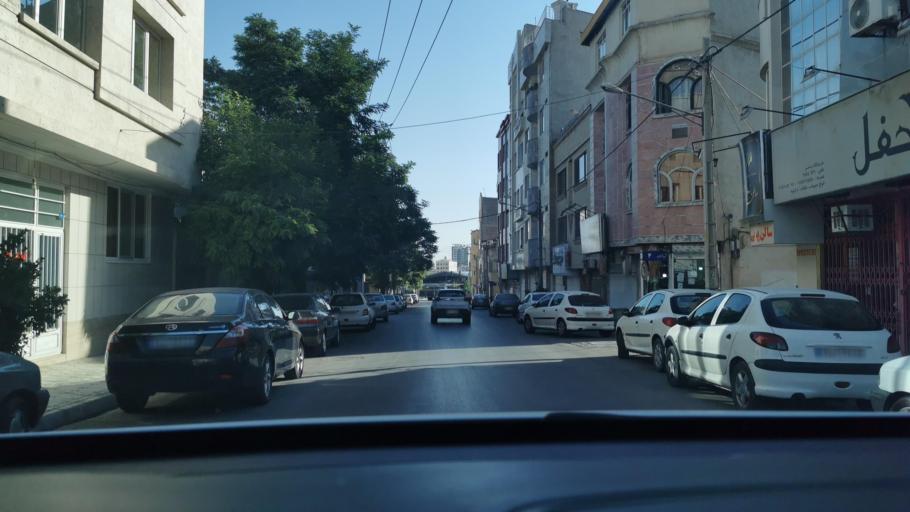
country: IR
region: Razavi Khorasan
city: Mashhad
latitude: 36.3085
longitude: 59.5110
